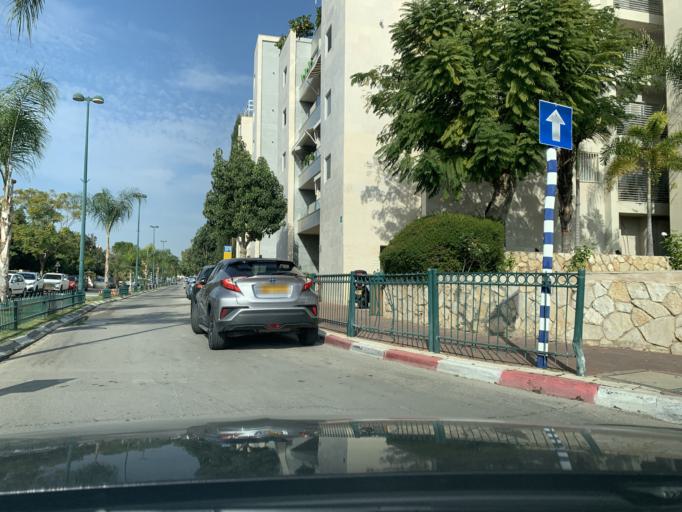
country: IL
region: Central District
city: Ganne Tiqwa
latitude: 32.0560
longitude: 34.8599
